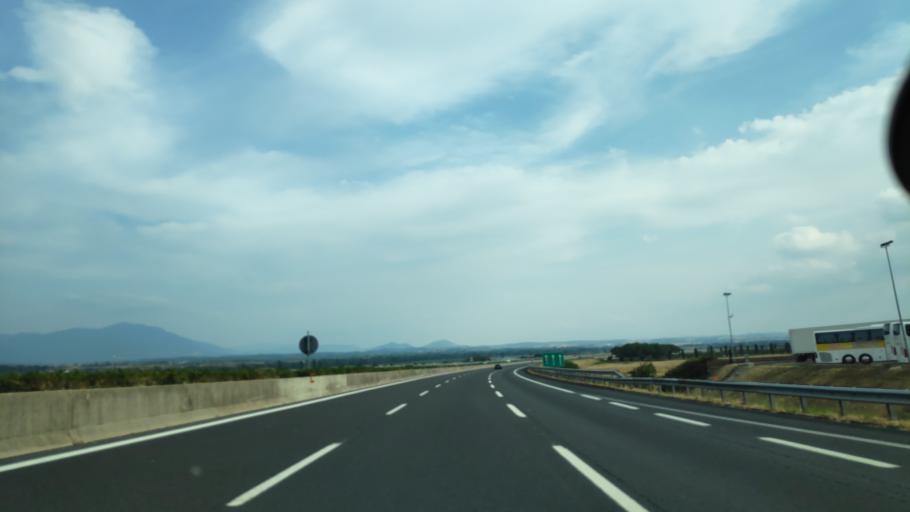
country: IT
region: Latium
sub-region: Citta metropolitana di Roma Capitale
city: Fiano Romano
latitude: 42.1582
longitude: 12.6226
